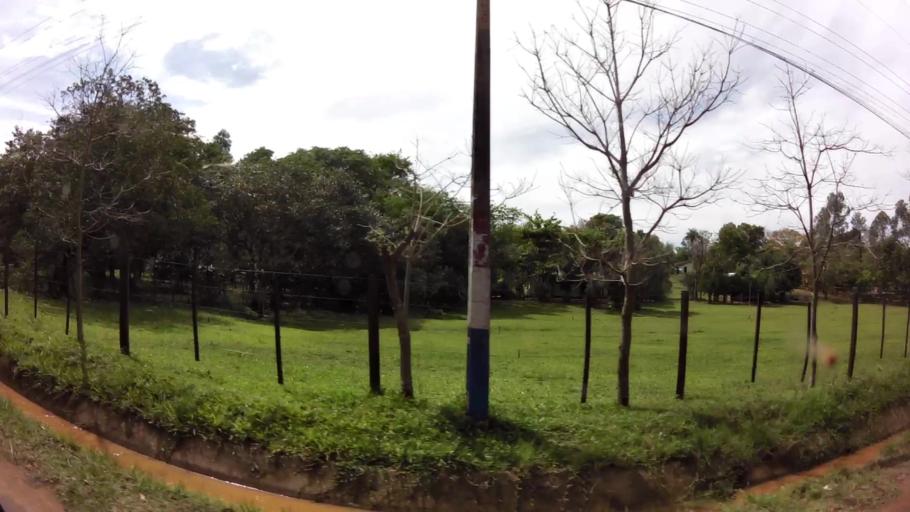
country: PY
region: Central
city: Limpio
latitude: -25.1789
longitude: -57.4425
